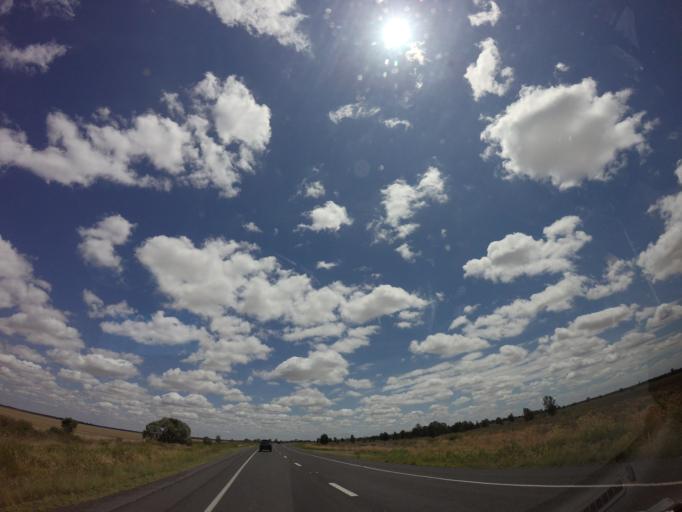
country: AU
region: New South Wales
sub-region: Moree Plains
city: Moree
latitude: -29.0222
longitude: 150.0596
